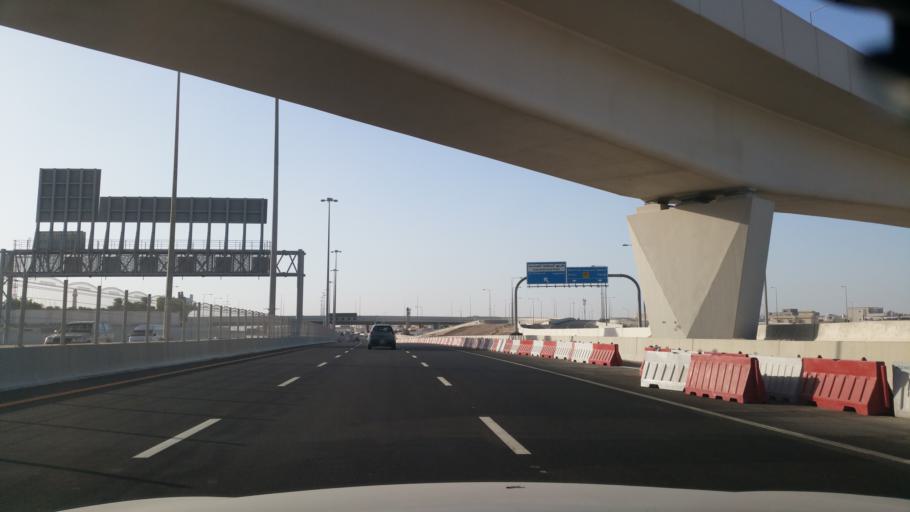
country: QA
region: Baladiyat ad Dawhah
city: Doha
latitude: 25.2345
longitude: 51.5268
